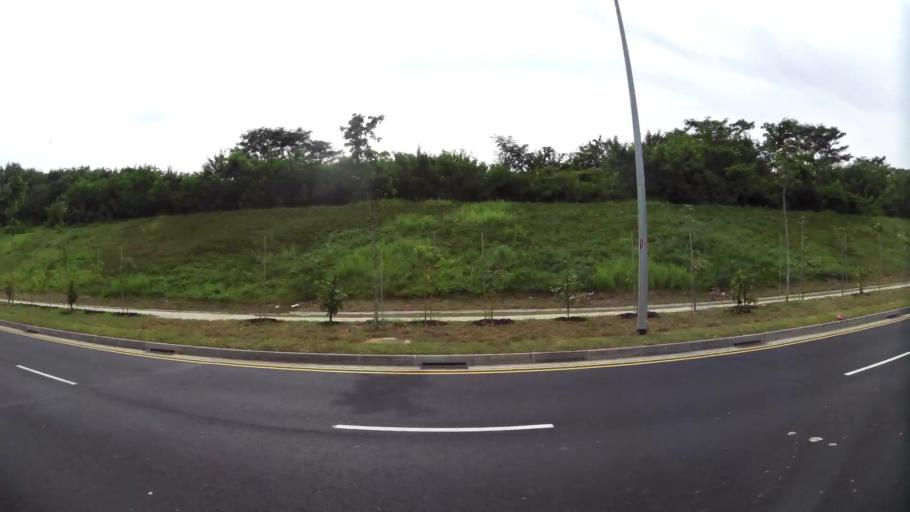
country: MY
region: Johor
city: Johor Bahru
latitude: 1.4271
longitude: 103.7564
